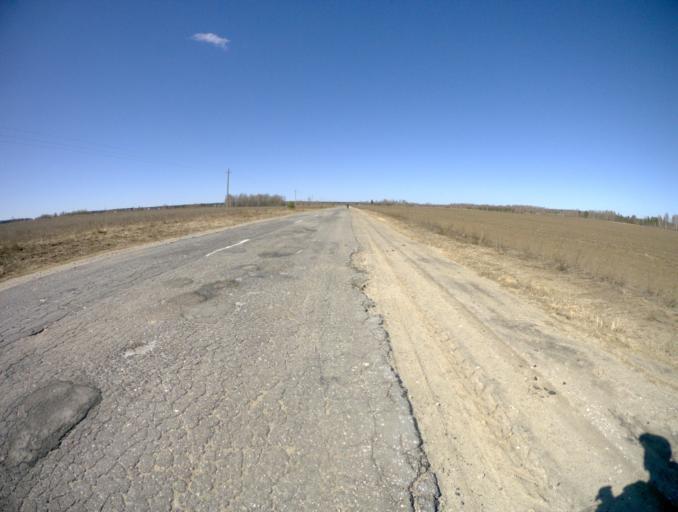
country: RU
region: Vladimir
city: Orgtrud
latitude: 56.3439
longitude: 40.7072
